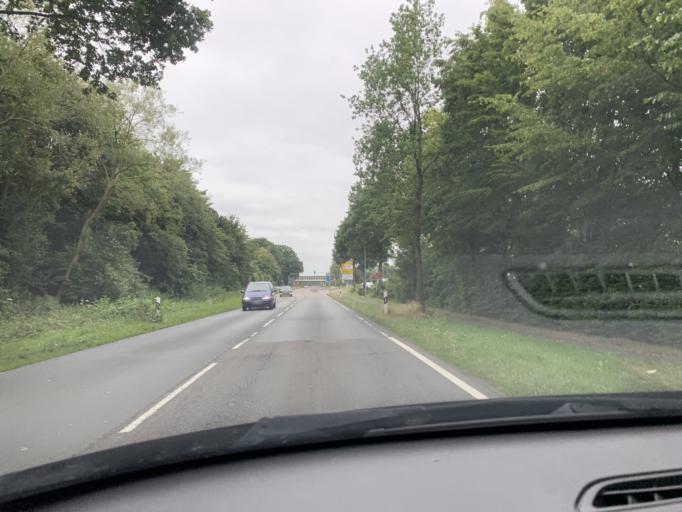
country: DE
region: Lower Saxony
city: Westerstede
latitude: 53.2644
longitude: 7.9437
